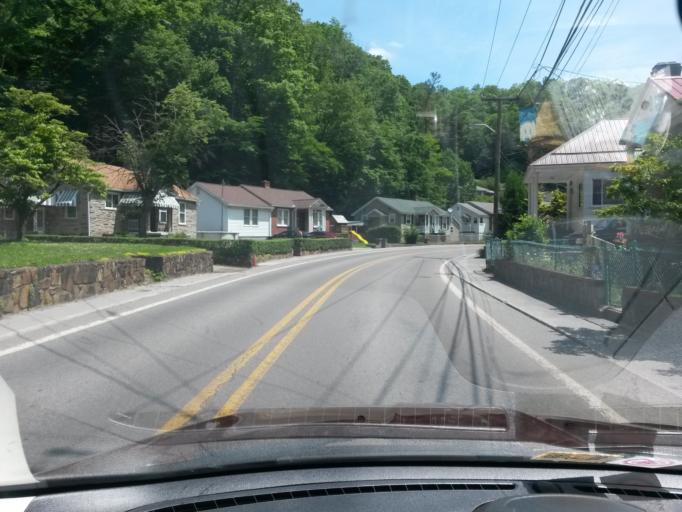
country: US
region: West Virginia
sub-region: McDowell County
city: Welch
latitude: 37.4401
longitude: -81.5855
